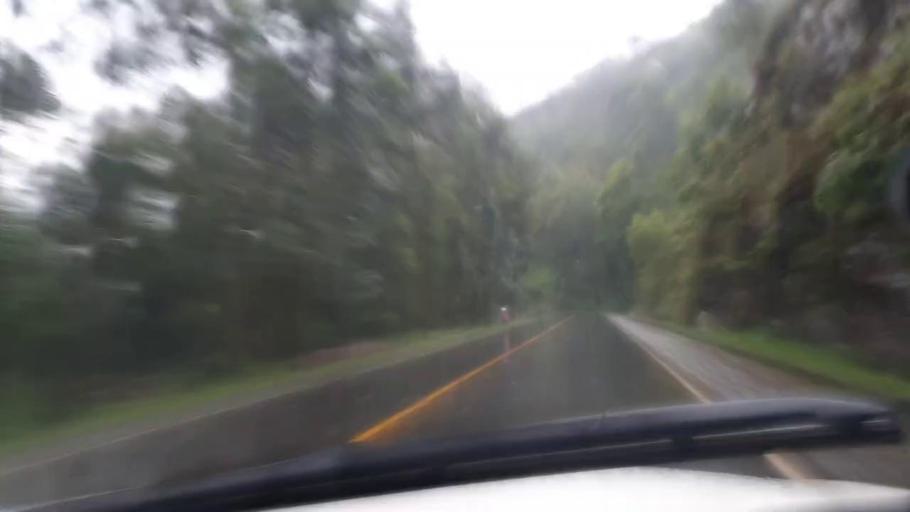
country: RW
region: Northern Province
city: Byumba
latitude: -1.6577
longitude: 29.8716
